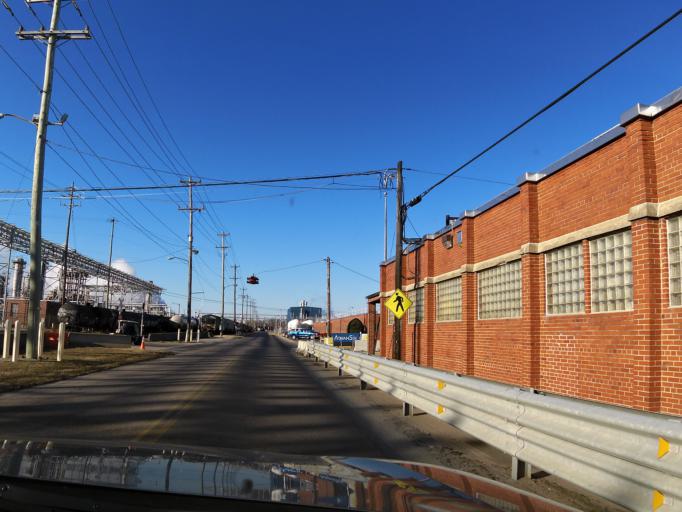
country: US
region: Virginia
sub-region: City of Hopewell
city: Hopewell
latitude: 37.3034
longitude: -77.2737
